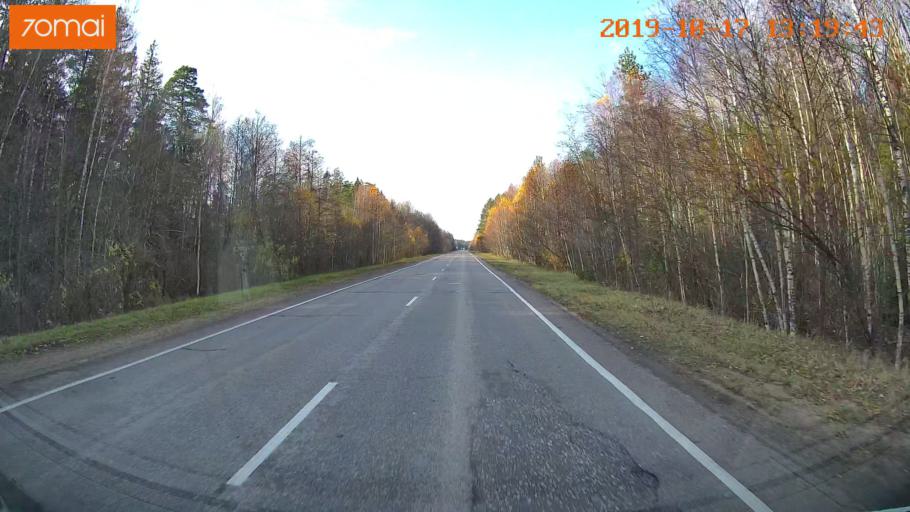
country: RU
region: Rjazan
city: Gus'-Zheleznyy
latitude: 55.0712
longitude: 41.0675
